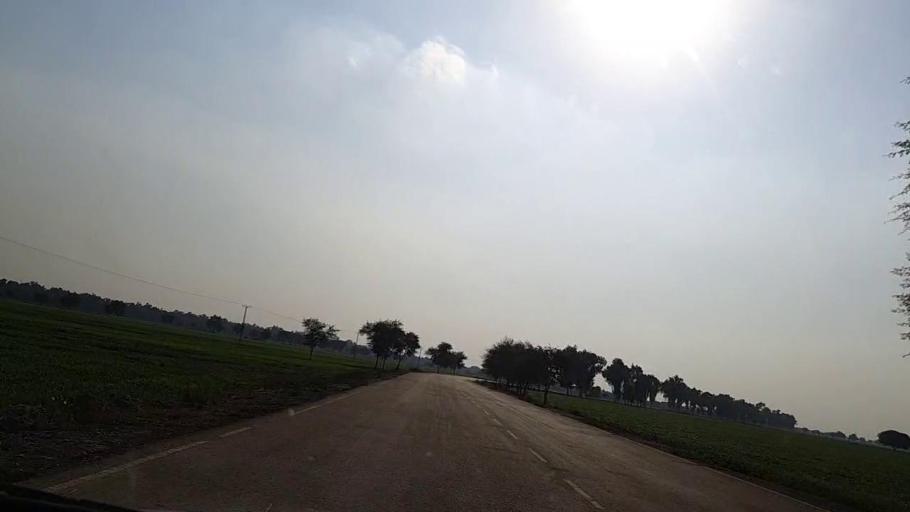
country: PK
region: Sindh
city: Sakrand
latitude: 26.1163
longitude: 68.2477
